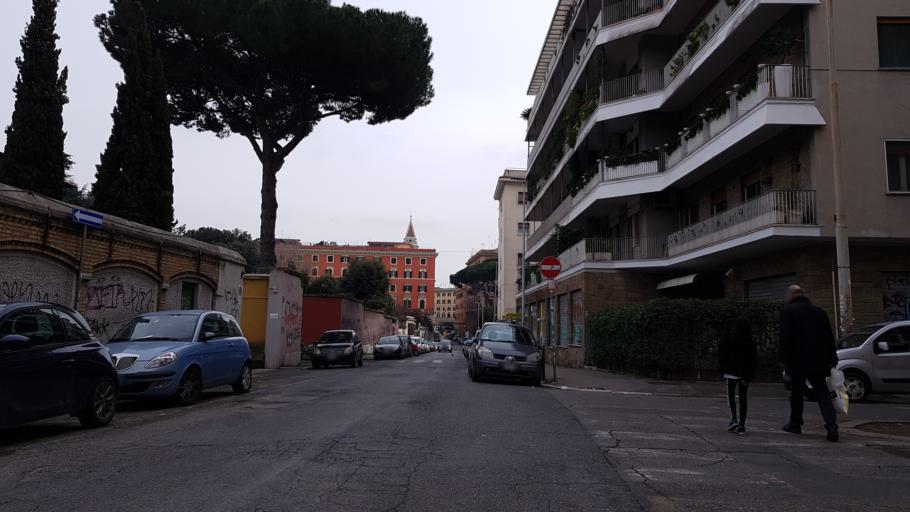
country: IT
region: Latium
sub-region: Citta metropolitana di Roma Capitale
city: Rome
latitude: 41.8994
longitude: 12.5126
